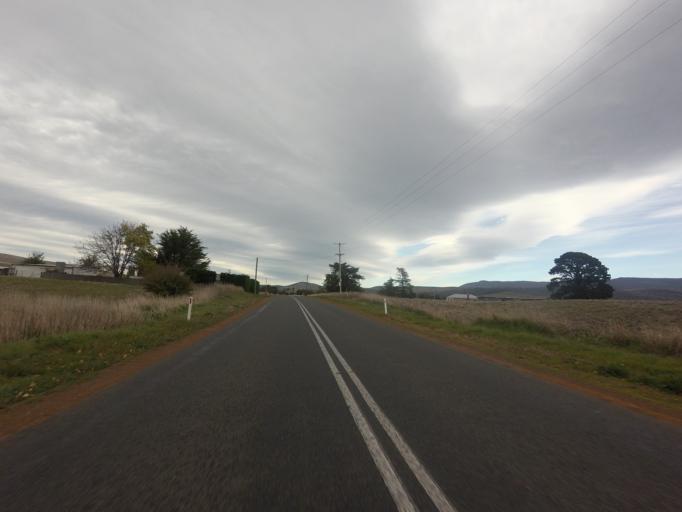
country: AU
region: Tasmania
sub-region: Derwent Valley
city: New Norfolk
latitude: -42.5241
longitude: 146.7506
